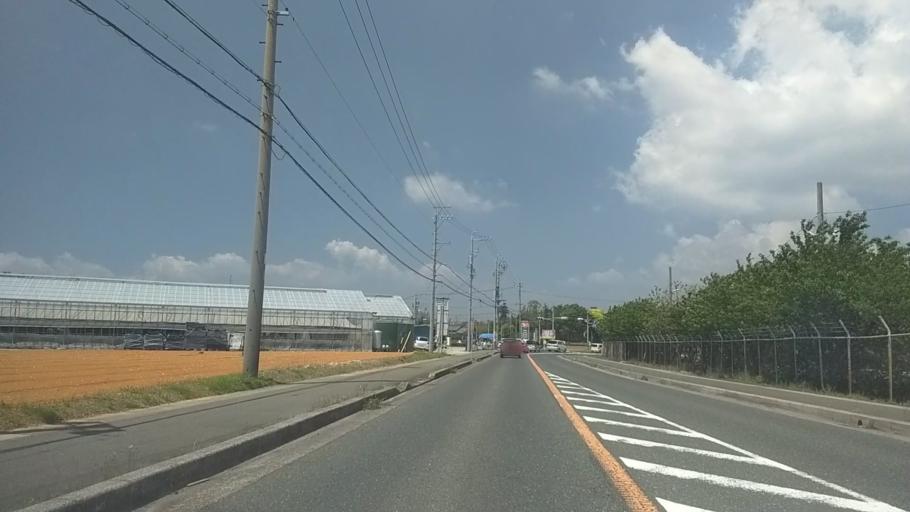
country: JP
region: Shizuoka
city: Hamamatsu
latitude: 34.7473
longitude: 137.6853
